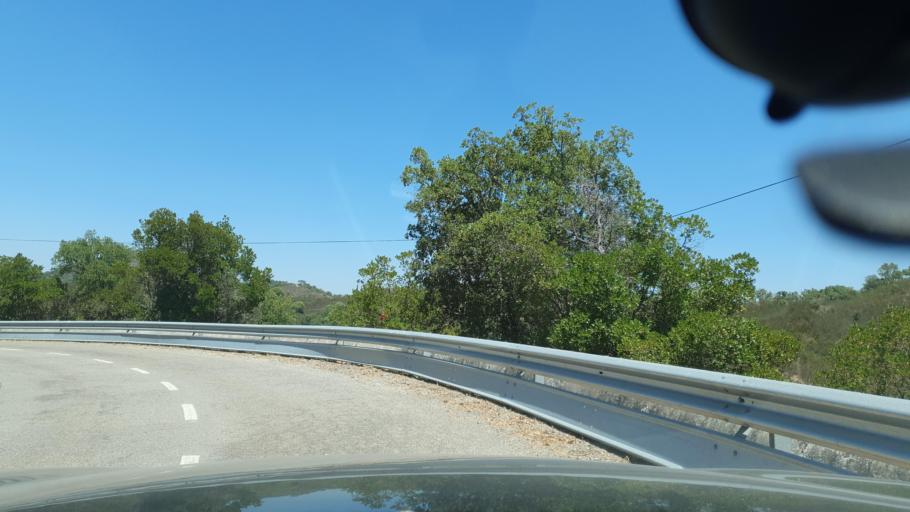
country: PT
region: Beja
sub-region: Odemira
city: Odemira
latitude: 37.6004
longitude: -8.5708
